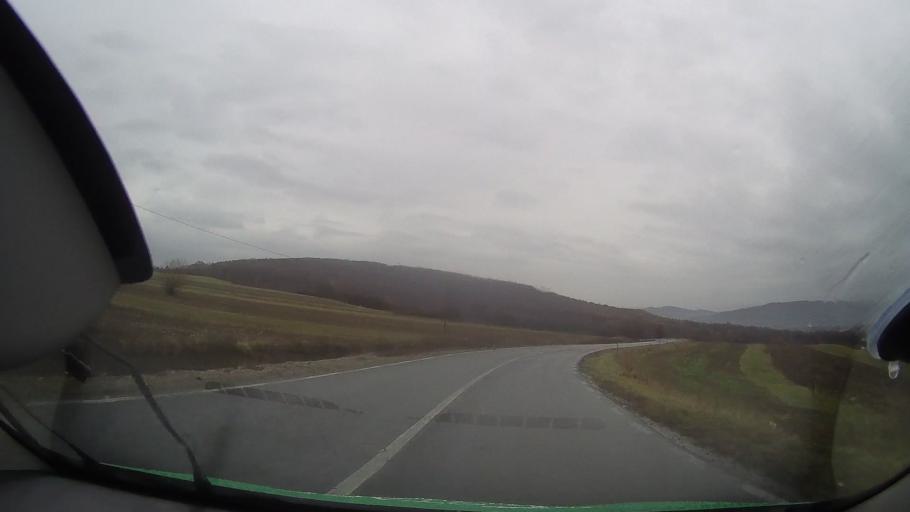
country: RO
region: Bihor
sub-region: Comuna Rabagani
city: Rabagani
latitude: 46.7285
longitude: 22.2348
